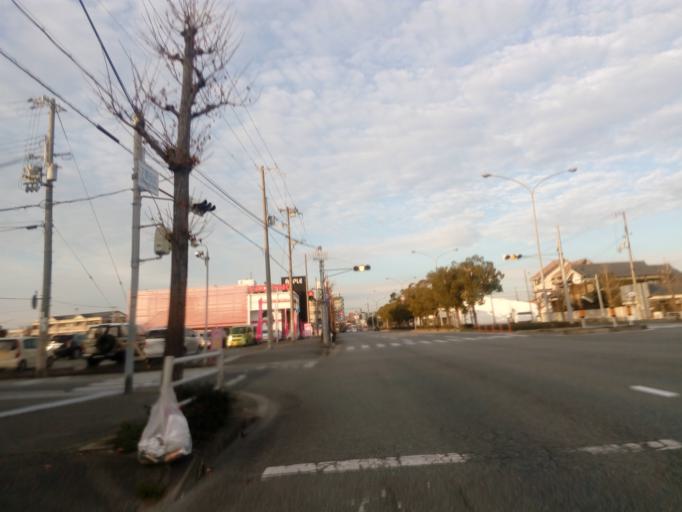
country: JP
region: Hyogo
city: Himeji
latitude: 34.8038
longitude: 134.6800
